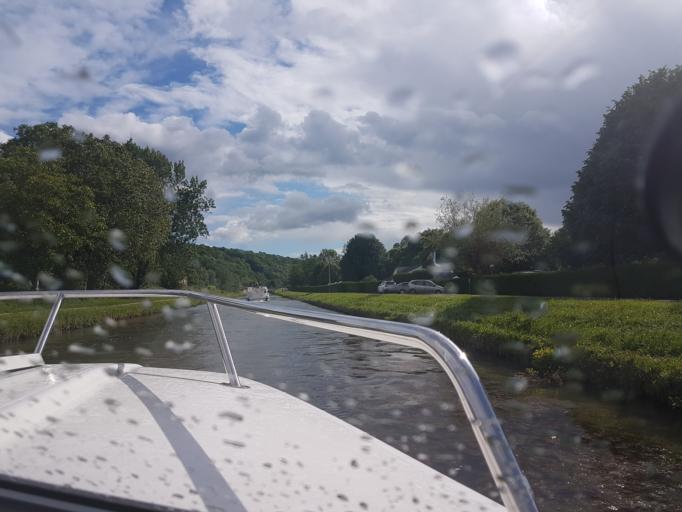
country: FR
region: Bourgogne
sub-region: Departement de la Nievre
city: Clamecy
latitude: 47.5366
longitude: 3.6339
